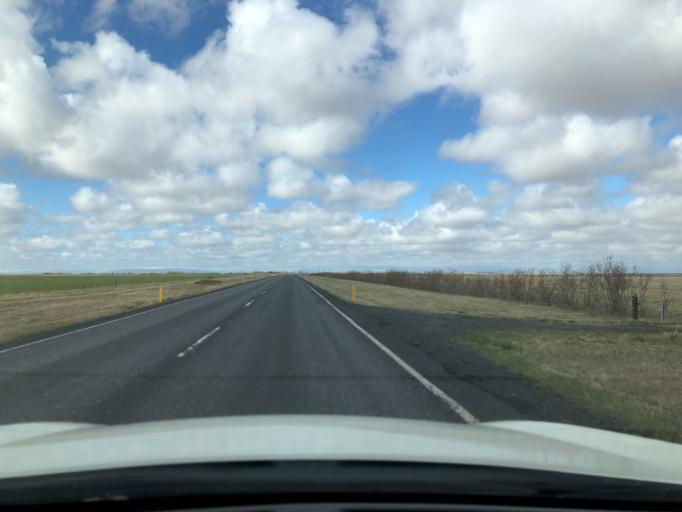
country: IS
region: South
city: Vestmannaeyjar
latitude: 63.7651
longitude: -20.2603
